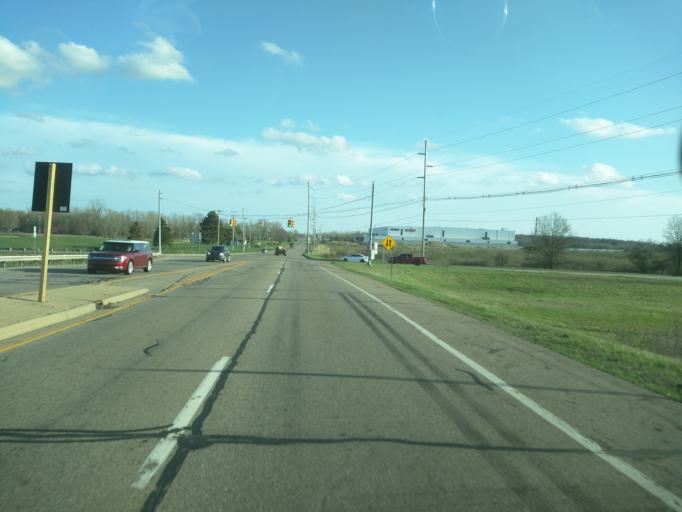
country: US
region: Michigan
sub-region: Eaton County
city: Waverly
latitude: 42.7182
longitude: -84.6425
